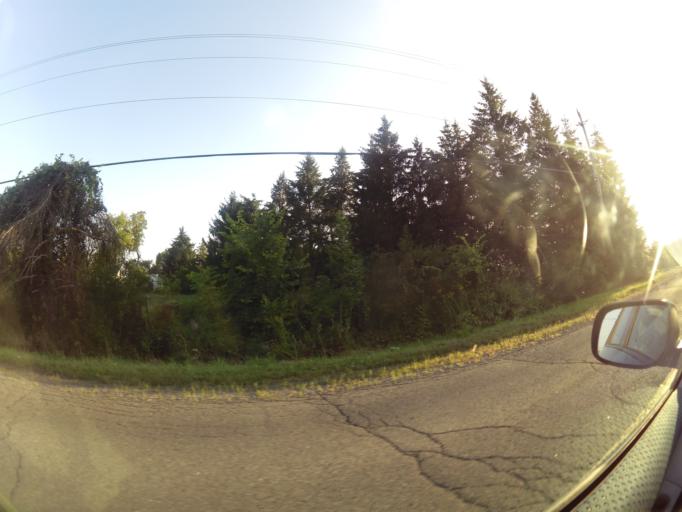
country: CA
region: Ontario
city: Clarence-Rockland
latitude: 45.4989
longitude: -75.4225
